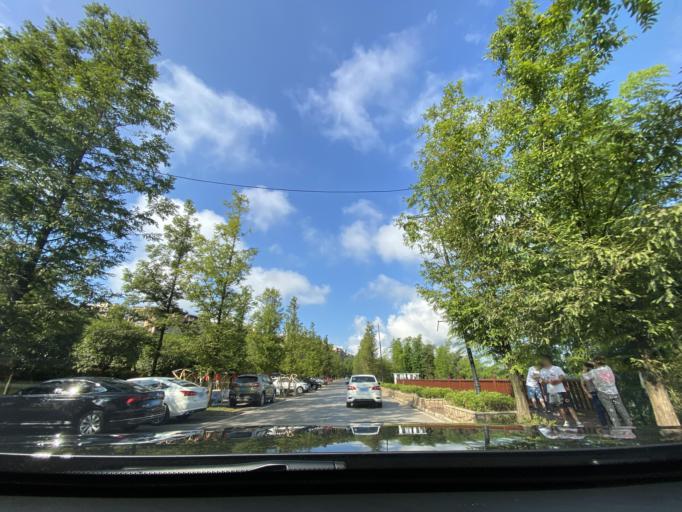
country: CN
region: Guizhou Sheng
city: Changqi
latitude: 28.5335
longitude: 105.9718
